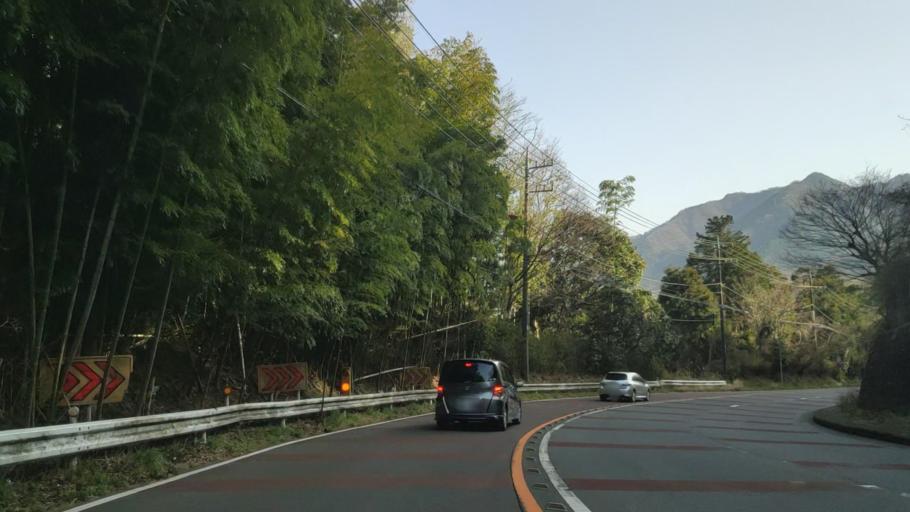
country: JP
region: Tokyo
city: Hachioji
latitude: 35.5511
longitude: 139.2640
